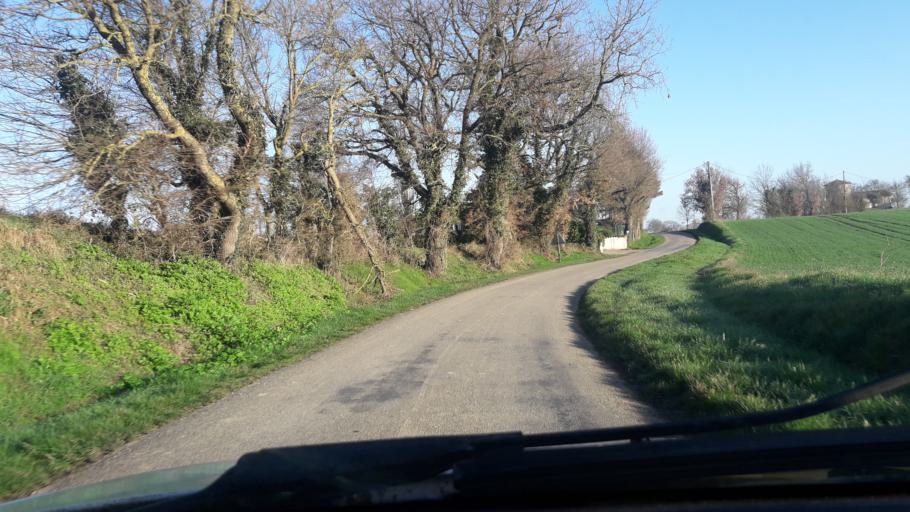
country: FR
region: Midi-Pyrenees
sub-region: Departement du Gers
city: Gimont
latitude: 43.6533
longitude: 0.9653
